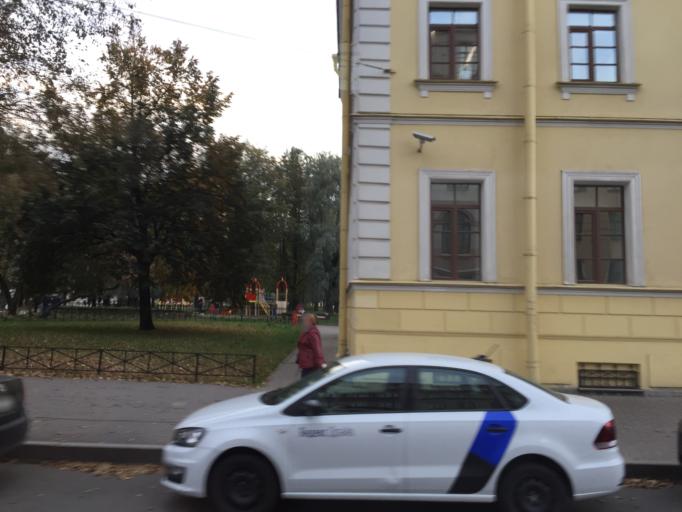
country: RU
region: St.-Petersburg
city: Centralniy
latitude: 59.9219
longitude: 30.3367
